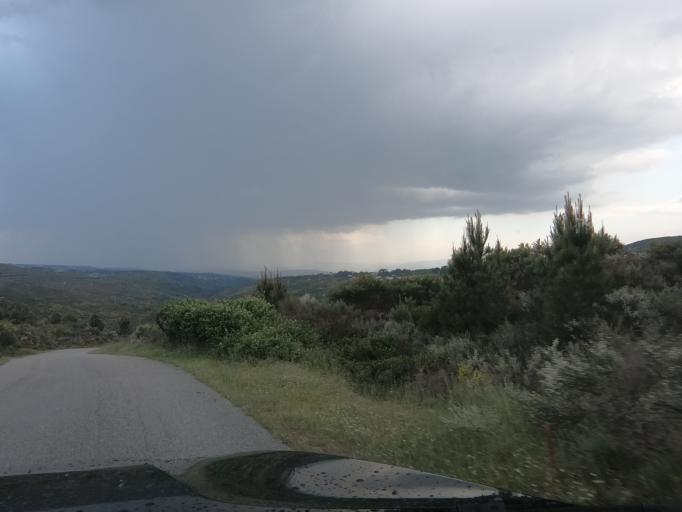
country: PT
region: Vila Real
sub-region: Vila Real
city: Vila Real
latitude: 41.3708
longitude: -7.7140
